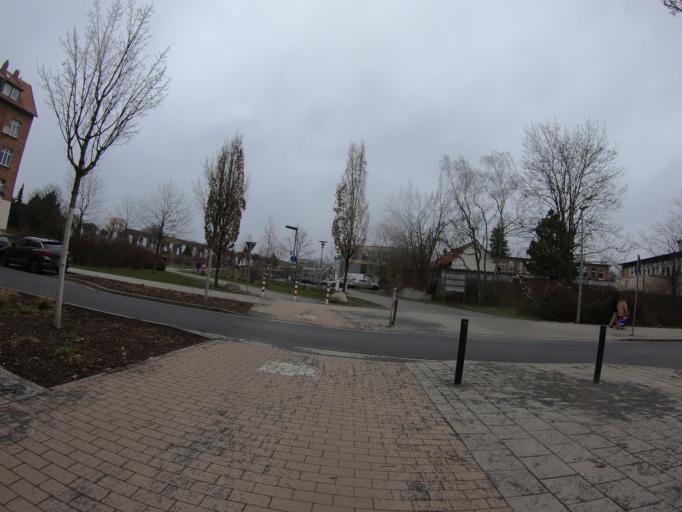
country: DE
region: Lower Saxony
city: Braunschweig
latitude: 52.2743
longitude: 10.5008
